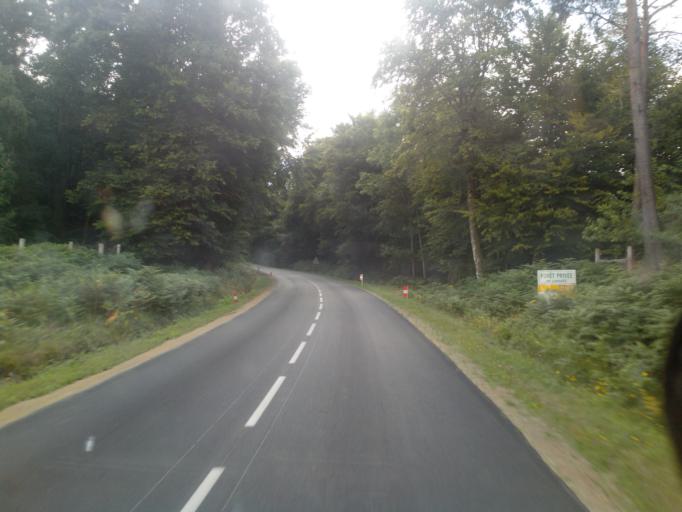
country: FR
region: Brittany
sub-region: Departement du Morbihan
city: Lanouee
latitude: 48.0452
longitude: -2.5322
